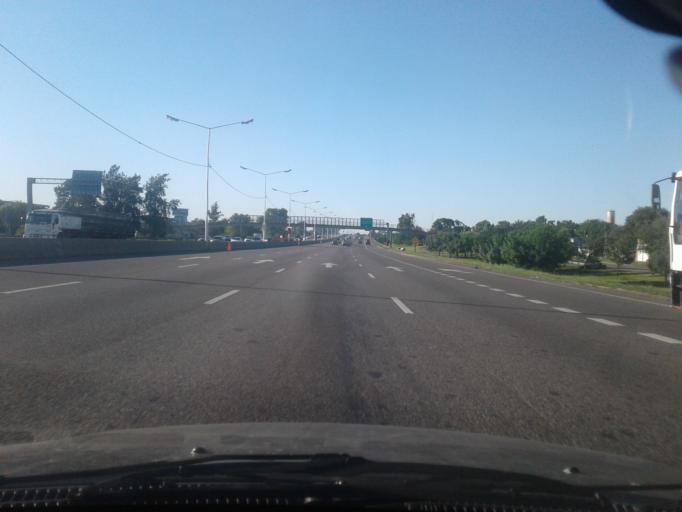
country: AR
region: Santa Fe
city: Granadero Baigorria
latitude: -32.9339
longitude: -60.7230
